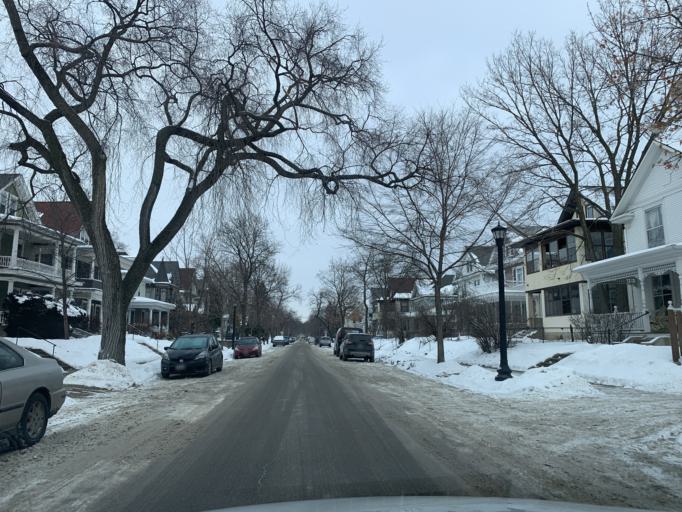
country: US
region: Minnesota
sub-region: Hennepin County
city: Minneapolis
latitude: 44.9543
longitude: -93.2918
